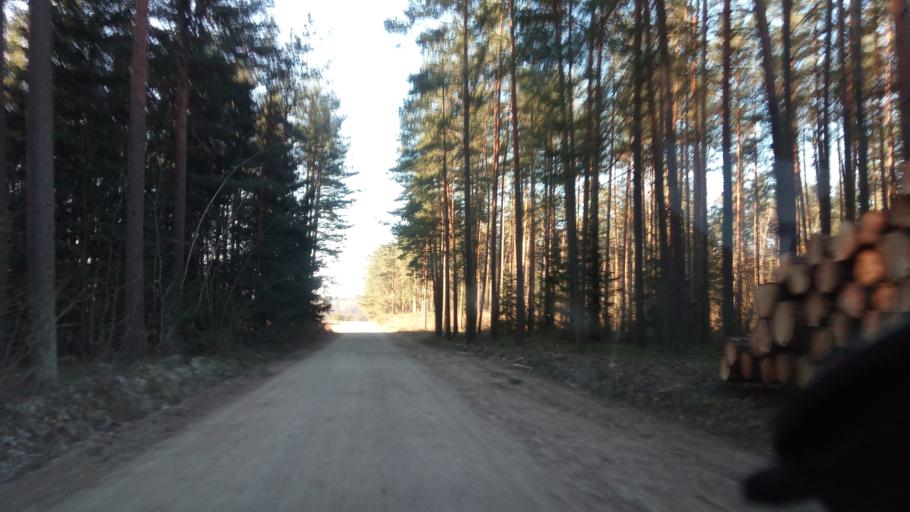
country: LT
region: Alytaus apskritis
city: Druskininkai
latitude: 54.1528
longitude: 23.9379
